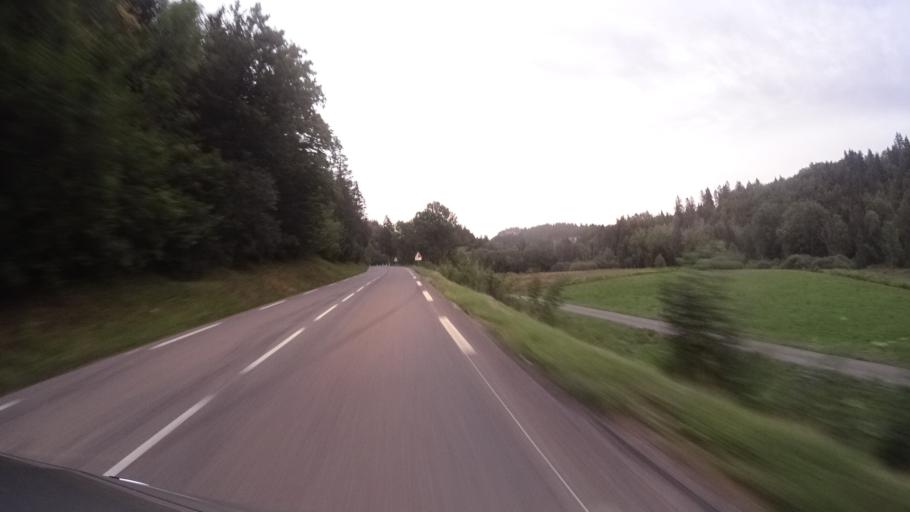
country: FR
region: Franche-Comte
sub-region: Departement du Jura
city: Morbier
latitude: 46.6678
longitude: 6.0908
